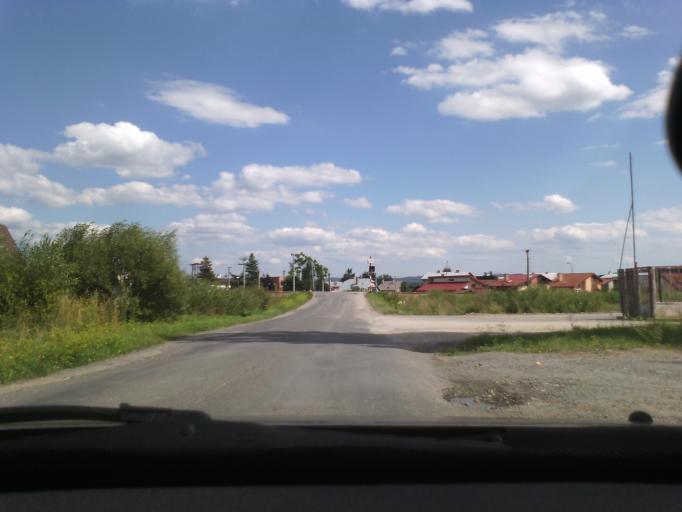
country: SK
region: Presovsky
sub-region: Okres Poprad
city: Poprad
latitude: 49.1201
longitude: 20.3503
